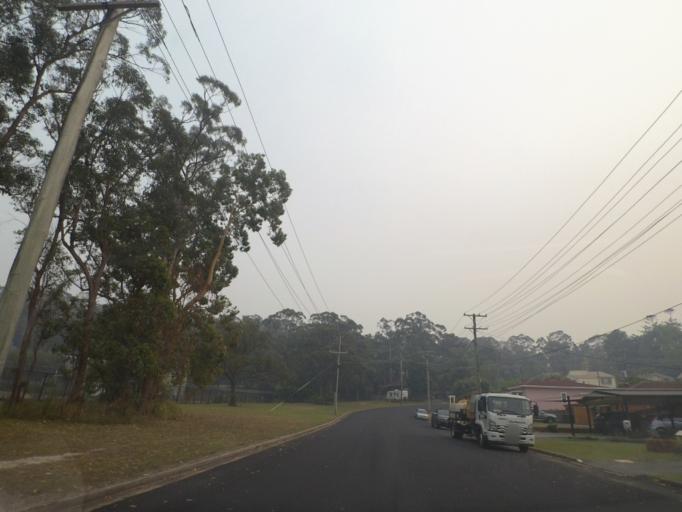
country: AU
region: New South Wales
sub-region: Coffs Harbour
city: Coffs Harbour
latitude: -30.3049
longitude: 153.1034
